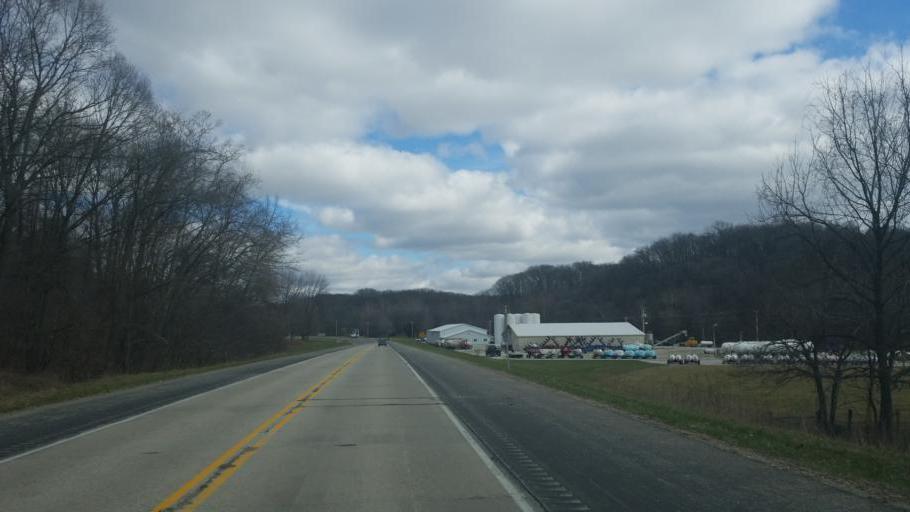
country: US
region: Indiana
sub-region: Parke County
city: Montezuma
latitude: 39.7749
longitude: -87.3229
